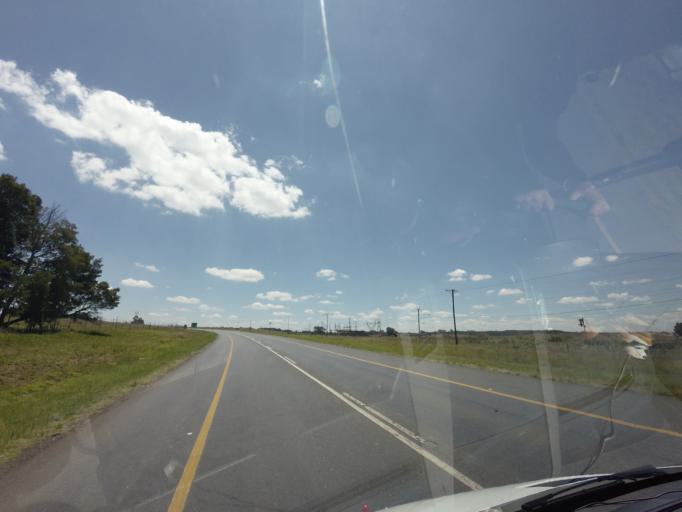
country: ZA
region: Mpumalanga
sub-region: Nkangala District Municipality
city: Belfast
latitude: -25.7162
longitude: 30.0749
